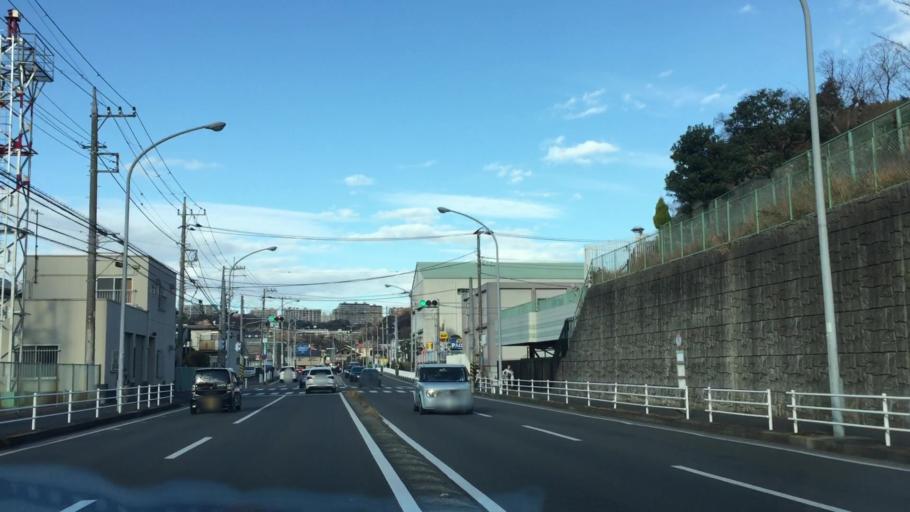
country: JP
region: Kanagawa
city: Zushi
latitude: 35.3407
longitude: 139.6113
